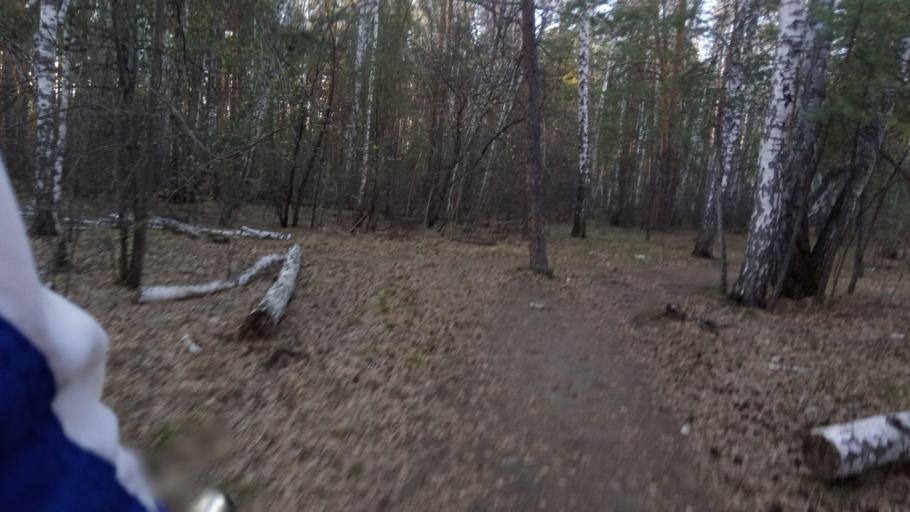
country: RU
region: Chelyabinsk
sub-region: Gorod Chelyabinsk
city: Chelyabinsk
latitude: 55.1417
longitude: 61.3395
